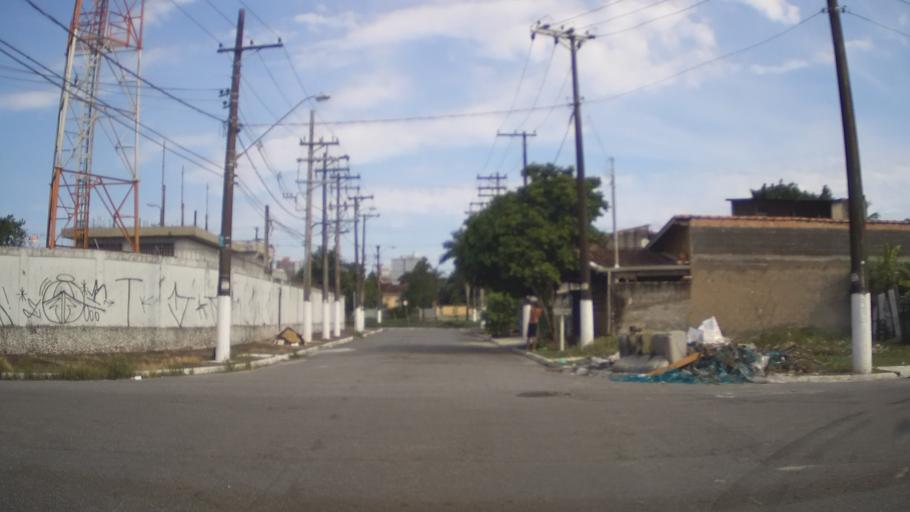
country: BR
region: Sao Paulo
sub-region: Praia Grande
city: Praia Grande
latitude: -24.0007
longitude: -46.4275
